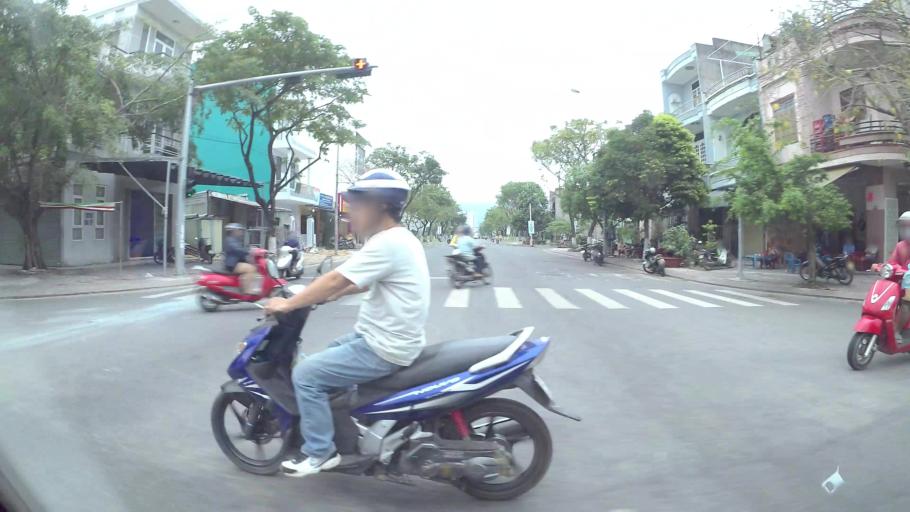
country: VN
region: Da Nang
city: Da Nang
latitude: 16.0879
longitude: 108.2380
